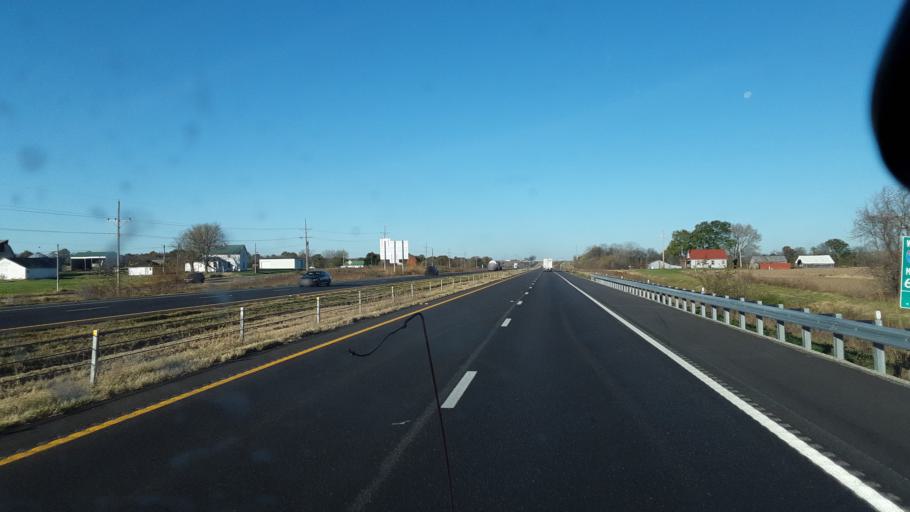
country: US
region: Missouri
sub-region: Saline County
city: Sweet Springs
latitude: 38.9781
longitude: -93.4426
